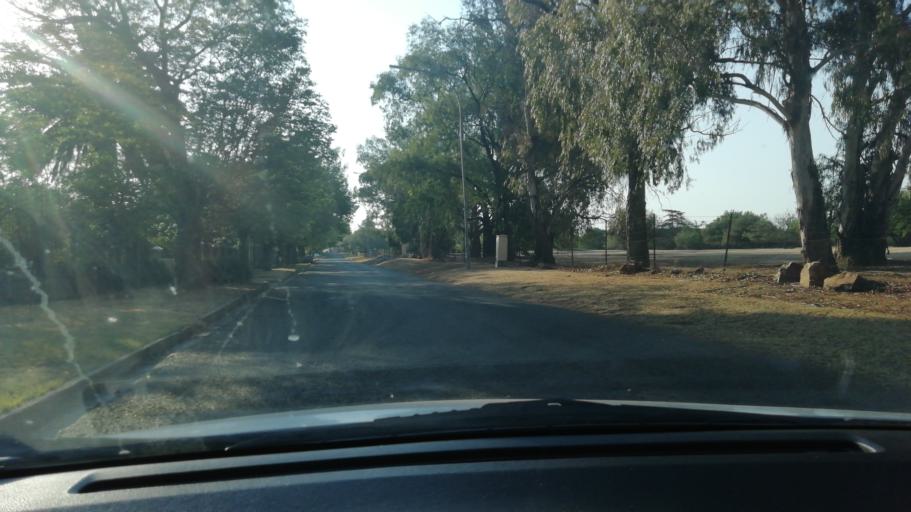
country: ZA
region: Gauteng
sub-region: Ekurhuleni Metropolitan Municipality
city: Benoni
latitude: -26.1880
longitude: 28.2951
